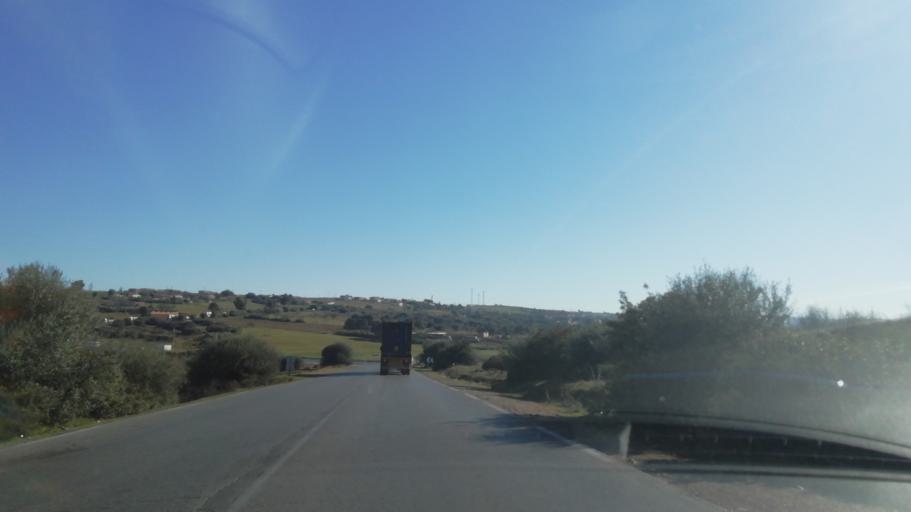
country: DZ
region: Relizane
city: Smala
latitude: 35.6866
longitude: 0.7961
